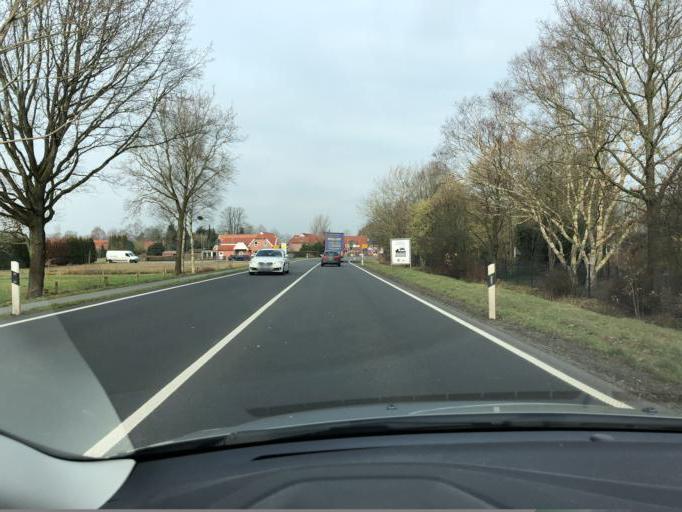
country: DE
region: Lower Saxony
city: Mittegrossefehn
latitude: 53.3935
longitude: 7.5720
